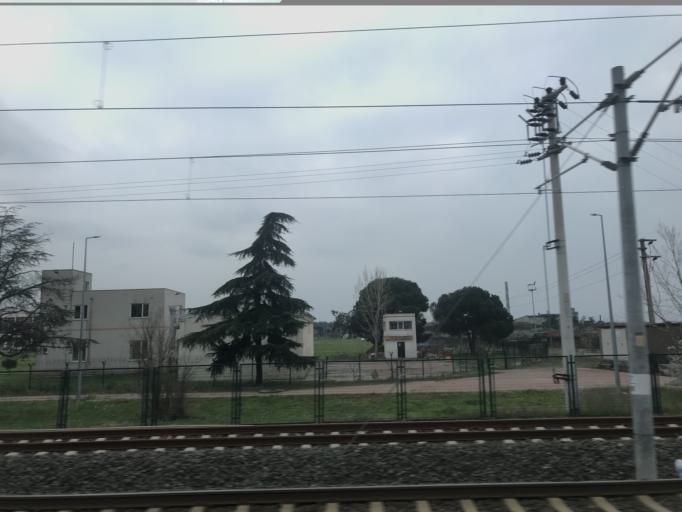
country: TR
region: Kocaeli
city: Darica
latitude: 40.8092
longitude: 29.3552
